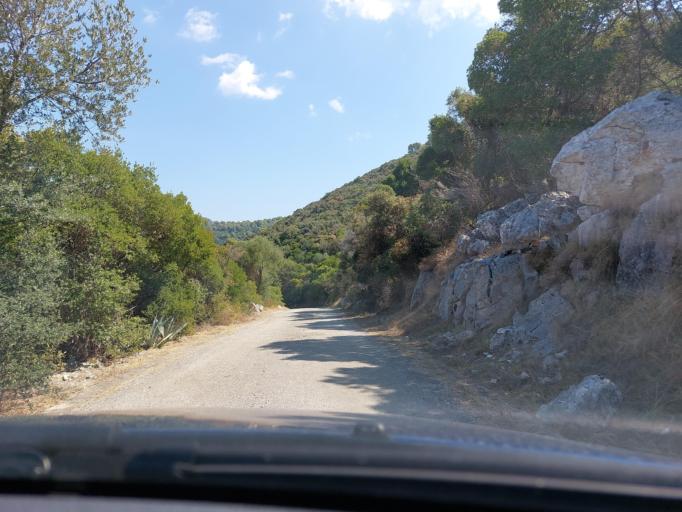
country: HR
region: Dubrovacko-Neretvanska
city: Smokvica
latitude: 42.7667
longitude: 16.8243
